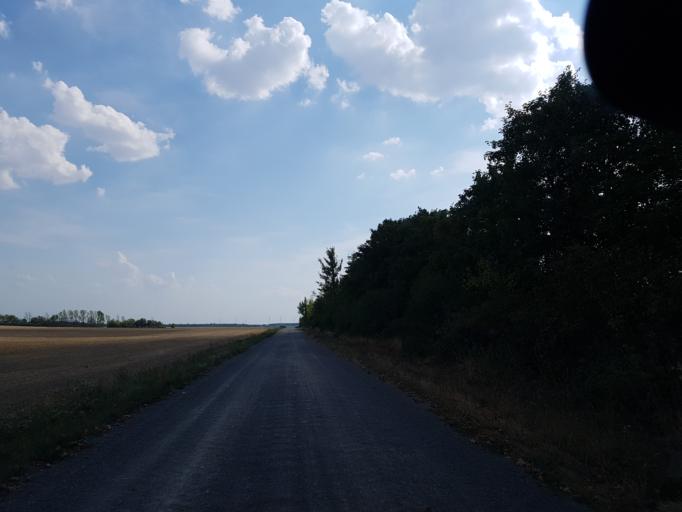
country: DE
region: Brandenburg
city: Treuenbrietzen
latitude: 51.9958
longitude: 12.8690
